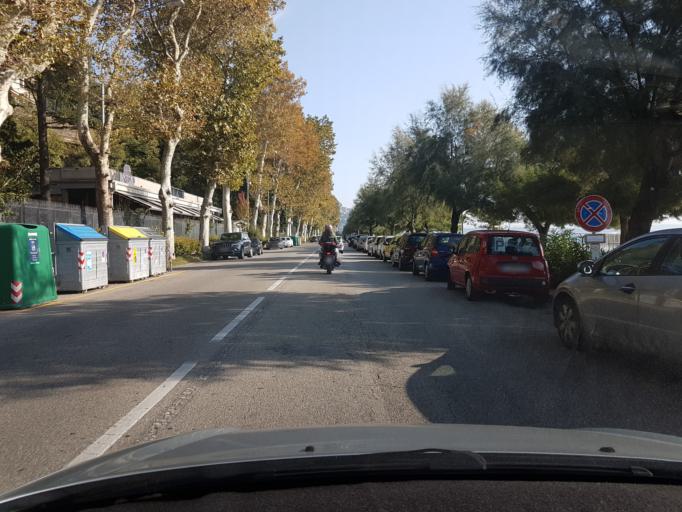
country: IT
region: Friuli Venezia Giulia
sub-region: Provincia di Trieste
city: Prosecco-Contovello
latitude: 45.6929
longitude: 13.7384
